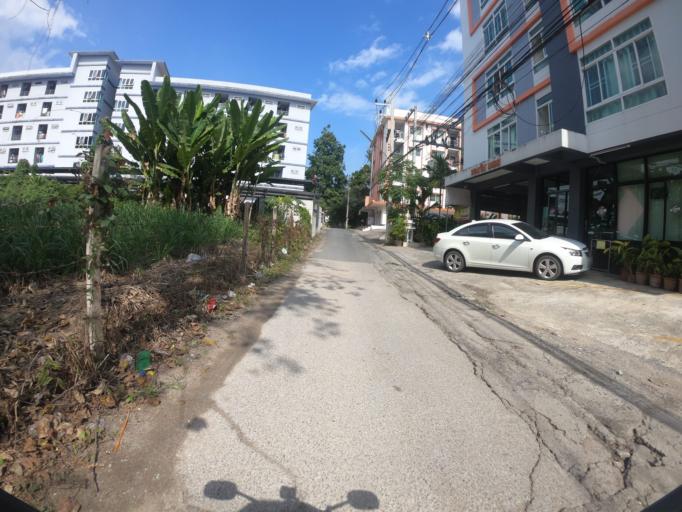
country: TH
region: Chiang Mai
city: Chiang Mai
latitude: 18.7879
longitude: 98.9576
